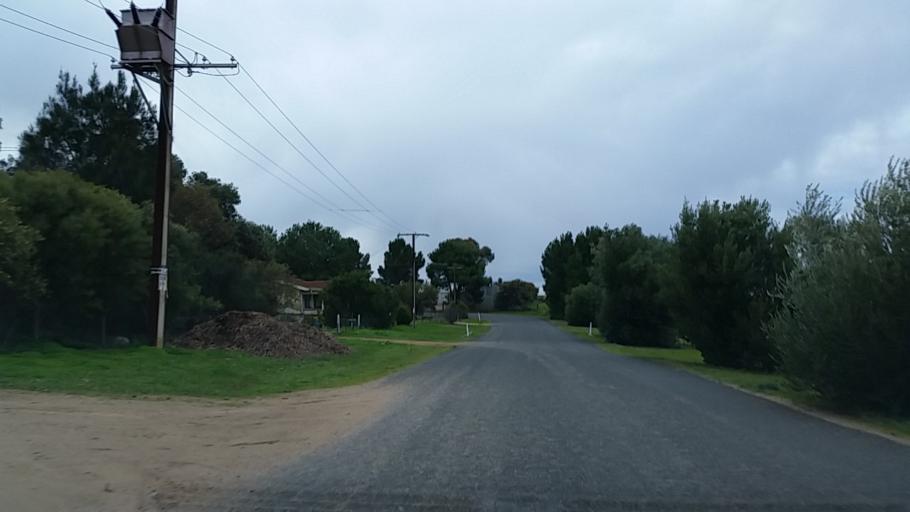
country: AU
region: South Australia
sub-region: Mid Murray
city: Mannum
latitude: -34.8528
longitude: 139.1625
